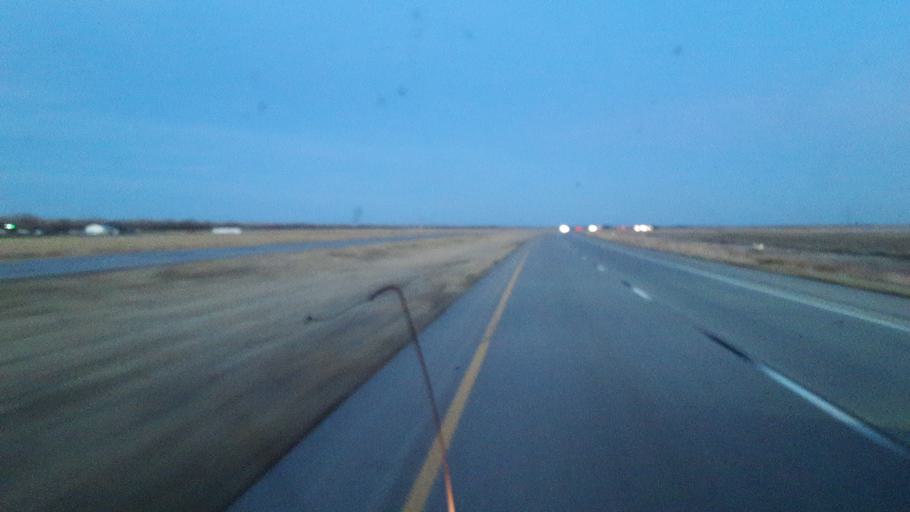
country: US
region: Nebraska
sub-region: Keith County
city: Ogallala
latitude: 41.1174
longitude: -101.5466
